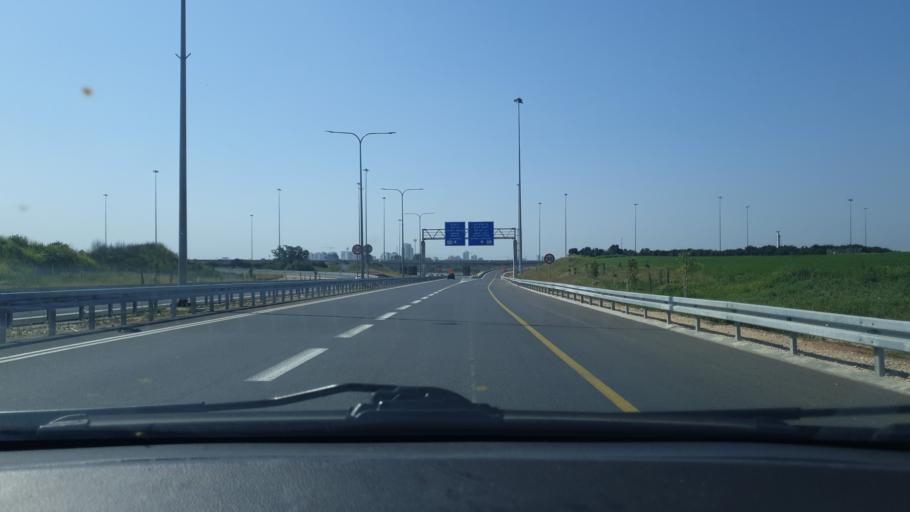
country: IL
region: Central District
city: Ramla
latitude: 31.9247
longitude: 34.8413
